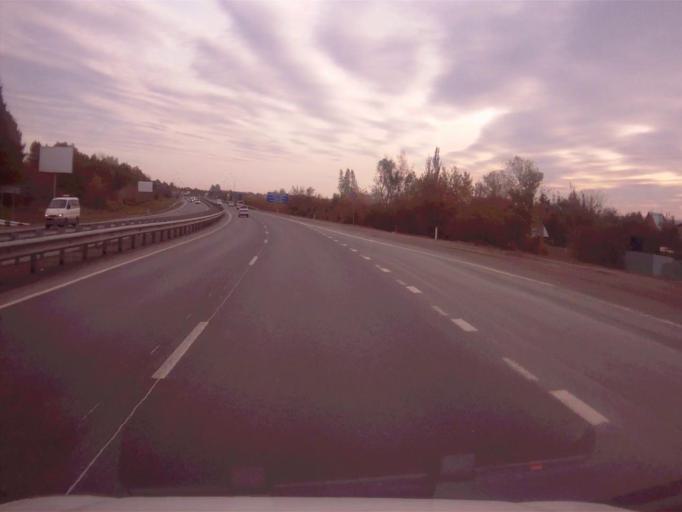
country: RU
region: Chelyabinsk
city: Novosineglazovskiy
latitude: 55.0355
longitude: 61.4420
